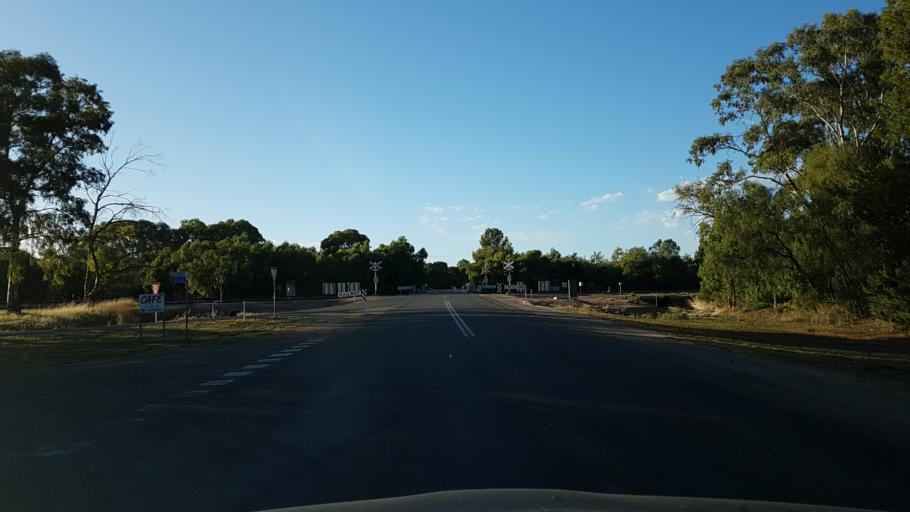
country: AU
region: South Australia
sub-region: Port Pirie City and Dists
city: Crystal Brook
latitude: -33.2757
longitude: 138.3562
